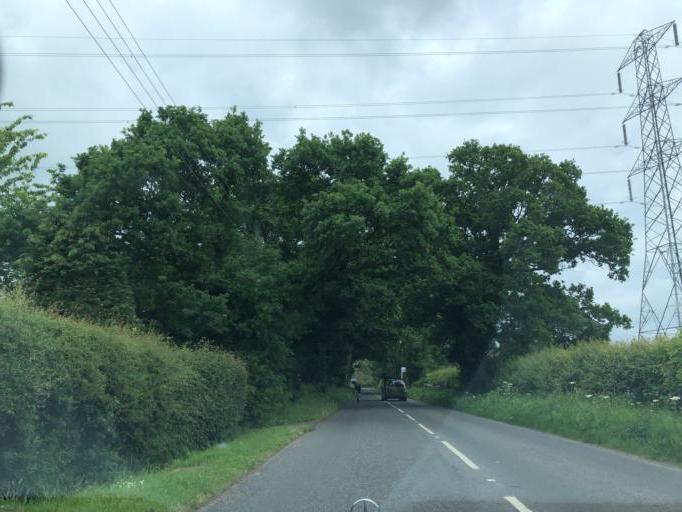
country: GB
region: England
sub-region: Solihull
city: Balsall Common
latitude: 52.3878
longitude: -1.6216
